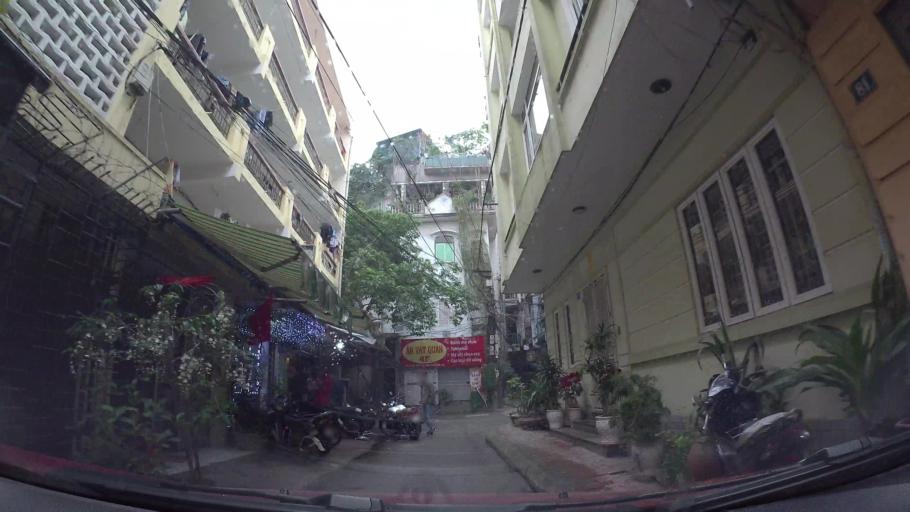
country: VN
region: Ha Noi
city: Dong Da
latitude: 21.0092
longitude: 105.8276
